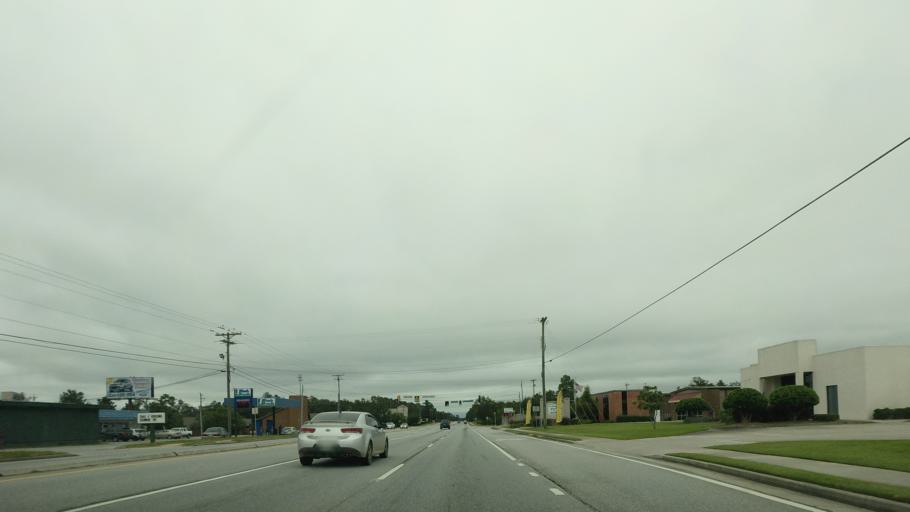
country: US
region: Georgia
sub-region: Lowndes County
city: Valdosta
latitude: 30.8890
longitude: -83.2710
